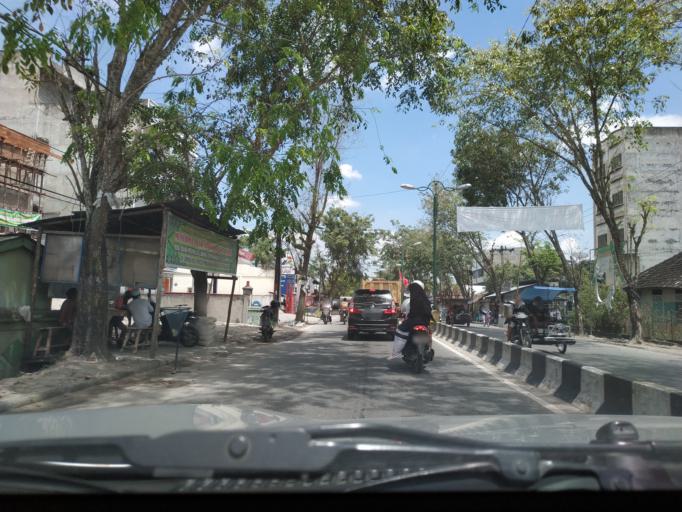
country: ID
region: North Sumatra
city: Tanjungbalai
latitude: 2.9539
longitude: 99.7940
